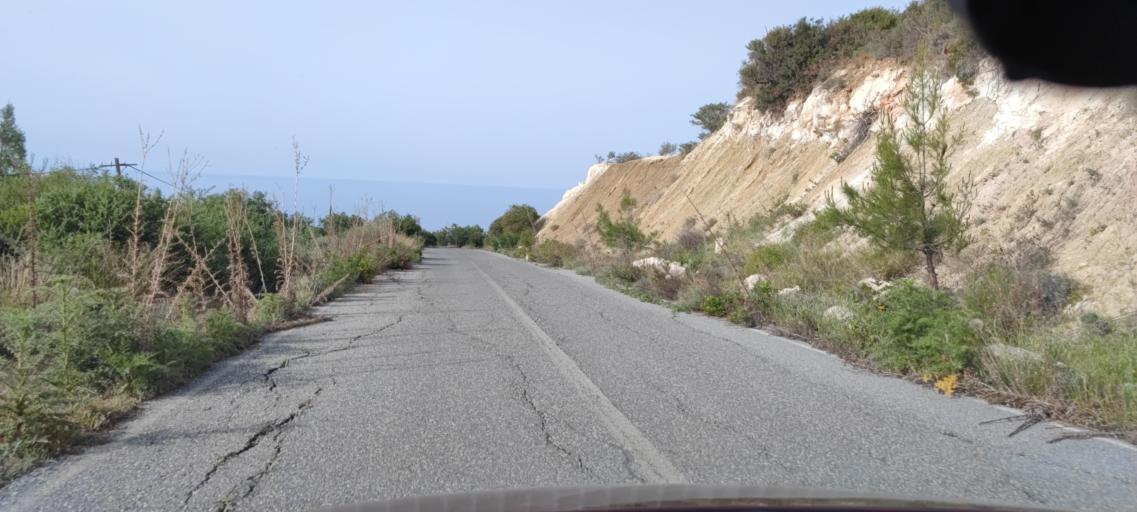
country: CY
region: Ammochostos
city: Trikomo
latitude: 35.4158
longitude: 33.9044
